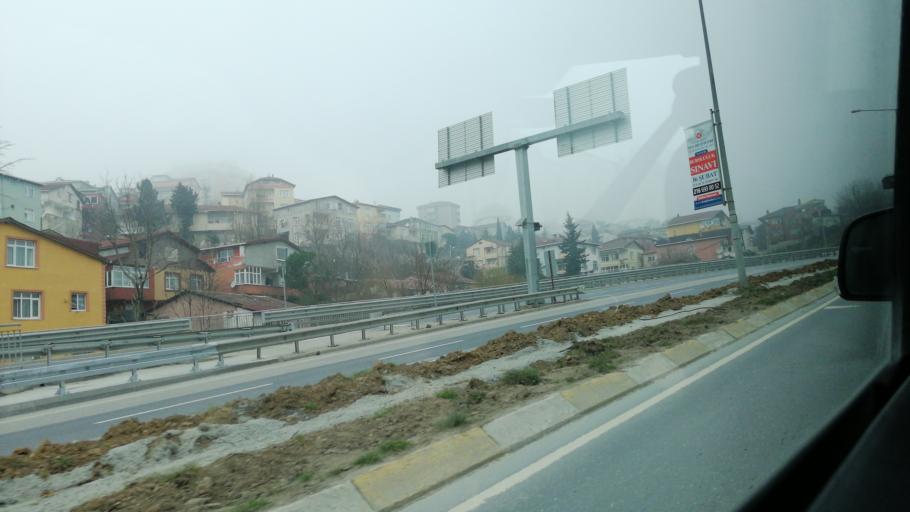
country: TR
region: Istanbul
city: Umraniye
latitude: 41.0863
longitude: 29.0855
